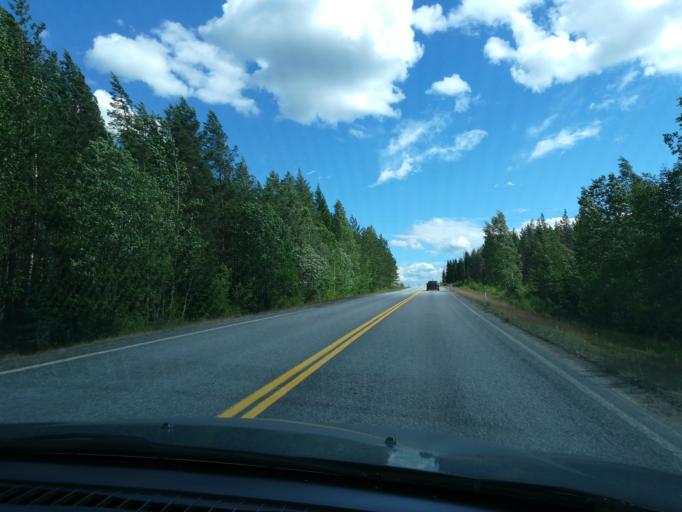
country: FI
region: Southern Savonia
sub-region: Mikkeli
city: Hirvensalmi
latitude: 61.6619
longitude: 26.9660
